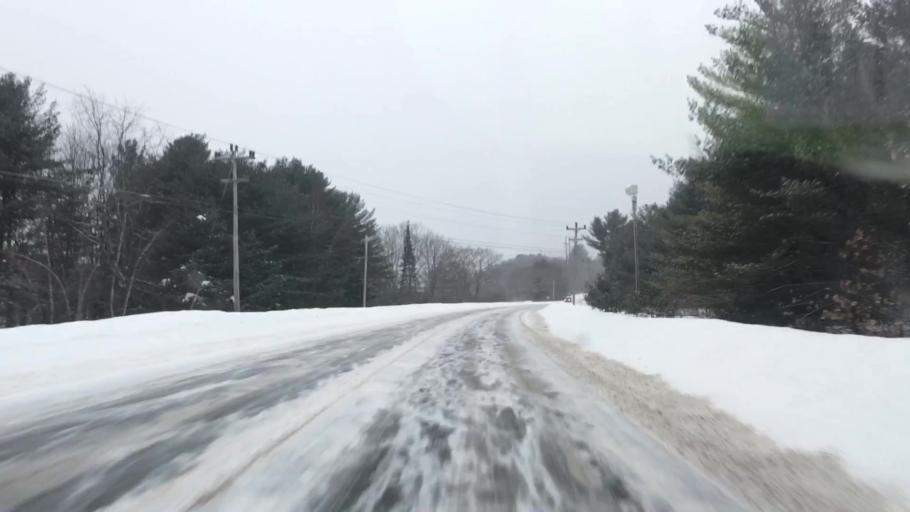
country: US
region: Maine
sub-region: Penobscot County
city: Medway
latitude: 45.5654
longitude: -68.4001
